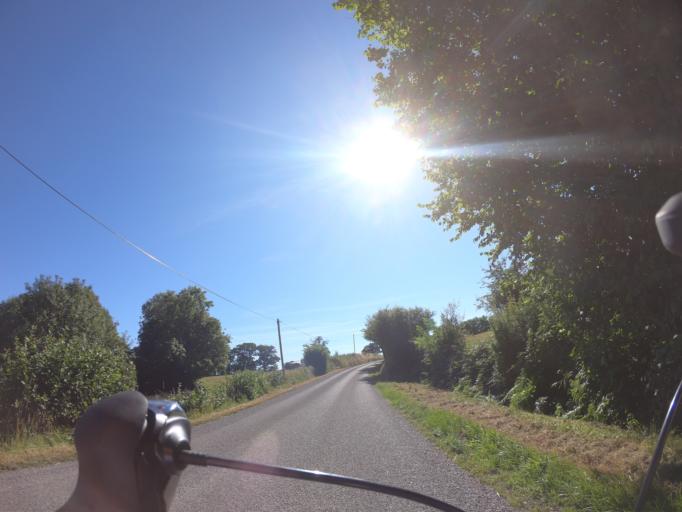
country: FR
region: Pays de la Loire
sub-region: Departement de la Mayenne
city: Pre-en-Pail
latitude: 48.5560
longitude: -0.1198
